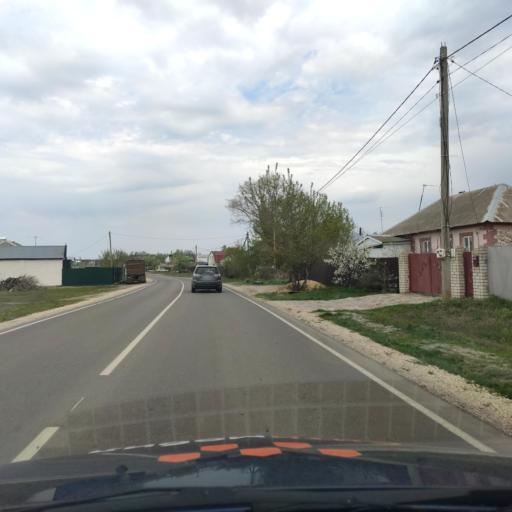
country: RU
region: Voronezj
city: Podgornoye
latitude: 51.8507
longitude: 39.1492
